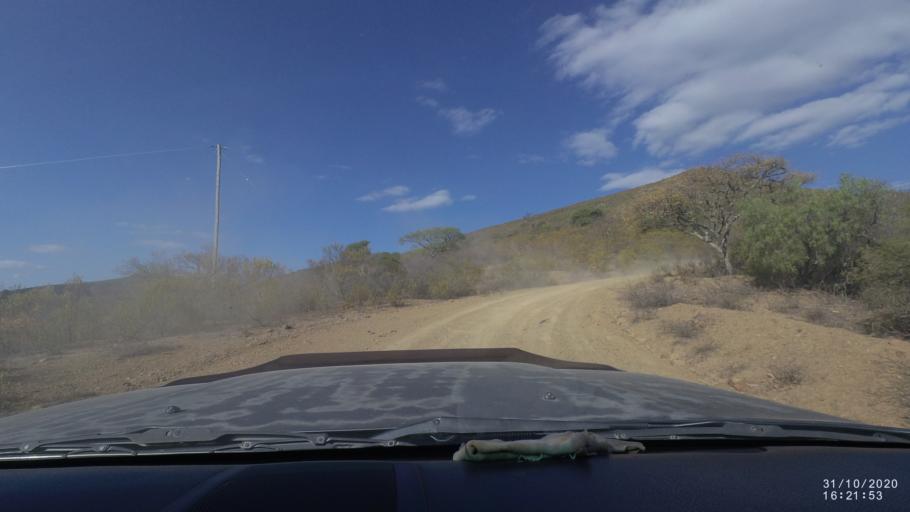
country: BO
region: Chuquisaca
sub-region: Provincia Zudanez
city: Mojocoya
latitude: -18.3987
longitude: -64.5950
